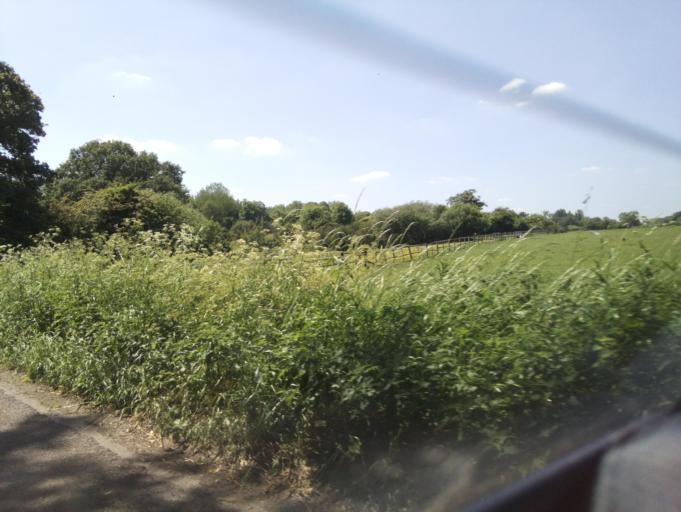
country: GB
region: England
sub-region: Wiltshire
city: Lyneham
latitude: 51.4742
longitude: -1.9561
